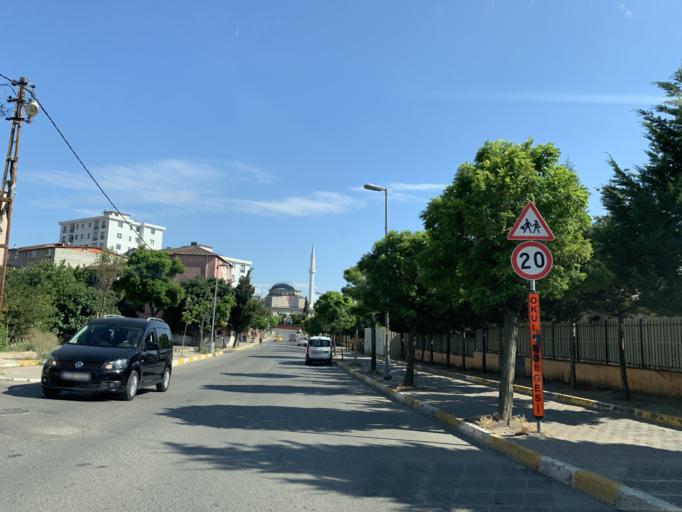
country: TR
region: Istanbul
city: Pendik
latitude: 40.8826
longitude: 29.2800
